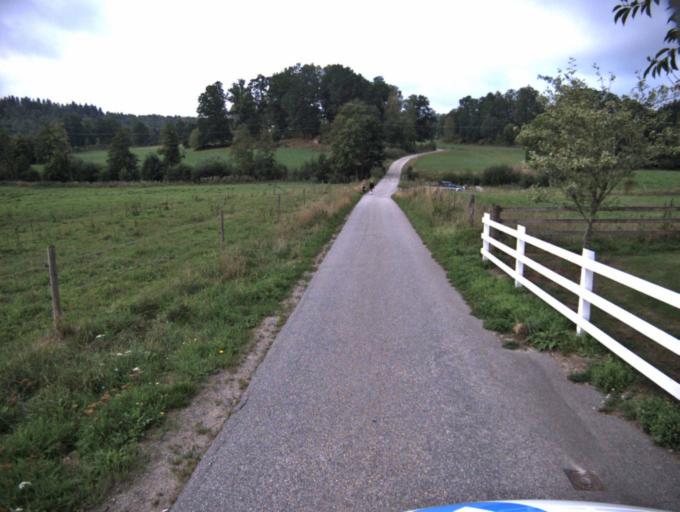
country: SE
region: Vaestra Goetaland
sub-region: Ulricehamns Kommun
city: Ulricehamn
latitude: 57.7374
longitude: 13.4212
